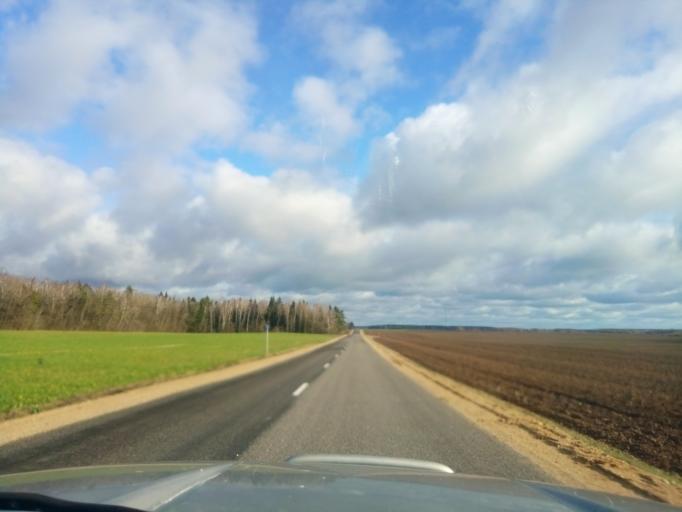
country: BY
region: Minsk
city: Tsimkavichy
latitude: 53.1383
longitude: 27.0022
